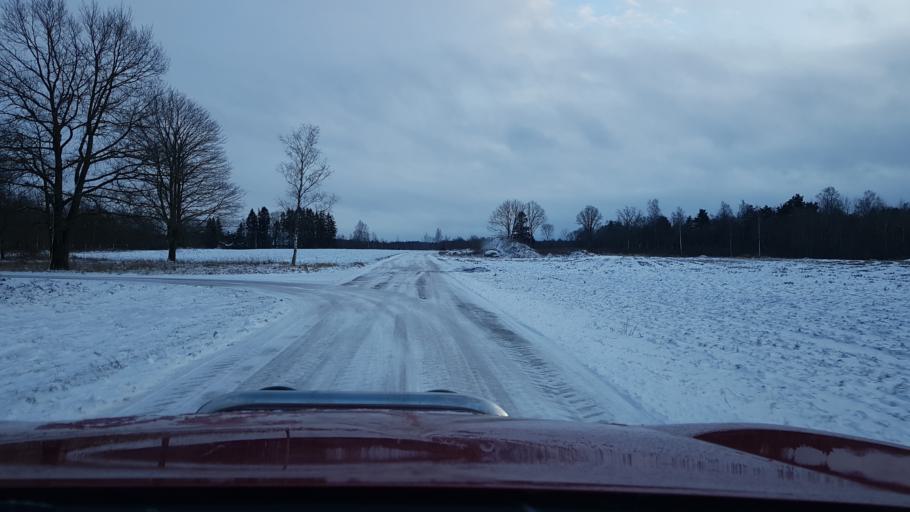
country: EE
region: Harju
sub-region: Maardu linn
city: Maardu
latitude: 59.4217
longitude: 25.0234
